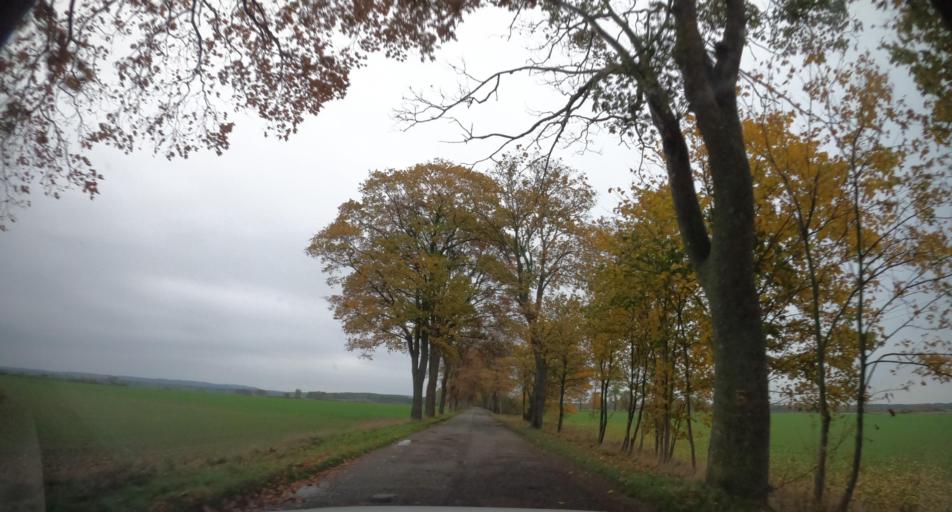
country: PL
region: West Pomeranian Voivodeship
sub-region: Powiat kamienski
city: Wolin
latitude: 53.9188
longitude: 14.6122
